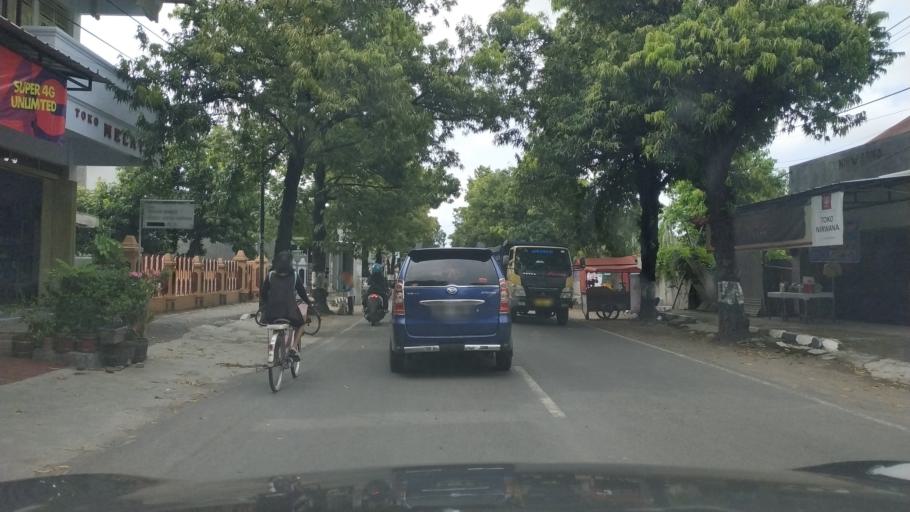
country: ID
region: Central Java
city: Pemalang
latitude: -6.8942
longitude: 109.3828
